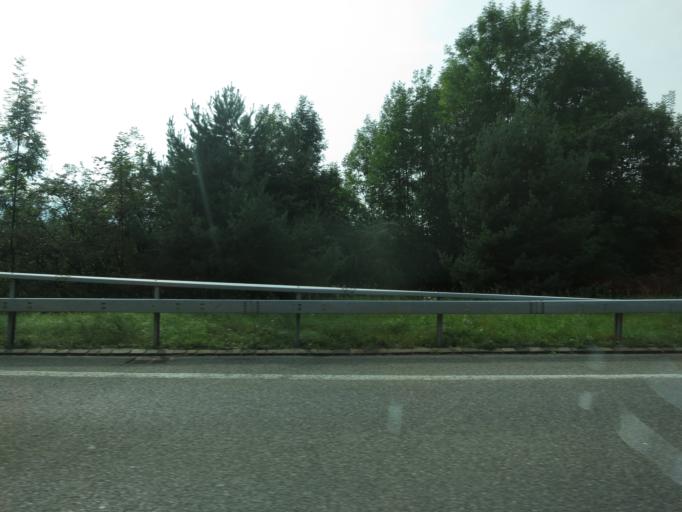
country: CH
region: Zurich
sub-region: Bezirk Hinwil
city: Rueti / Dorfzentrum, Suedl. Teil
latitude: 47.2309
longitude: 8.8663
